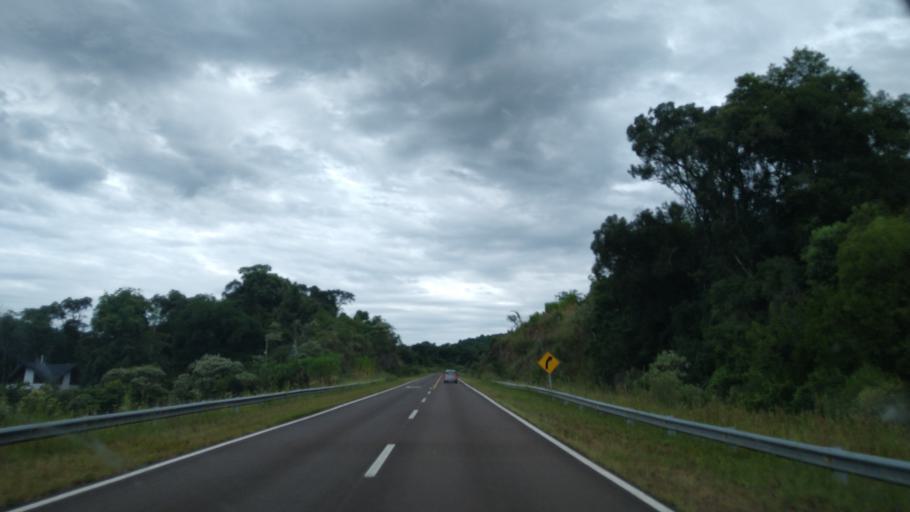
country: AR
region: Misiones
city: Bernardo de Irigoyen
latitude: -26.3239
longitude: -53.7561
